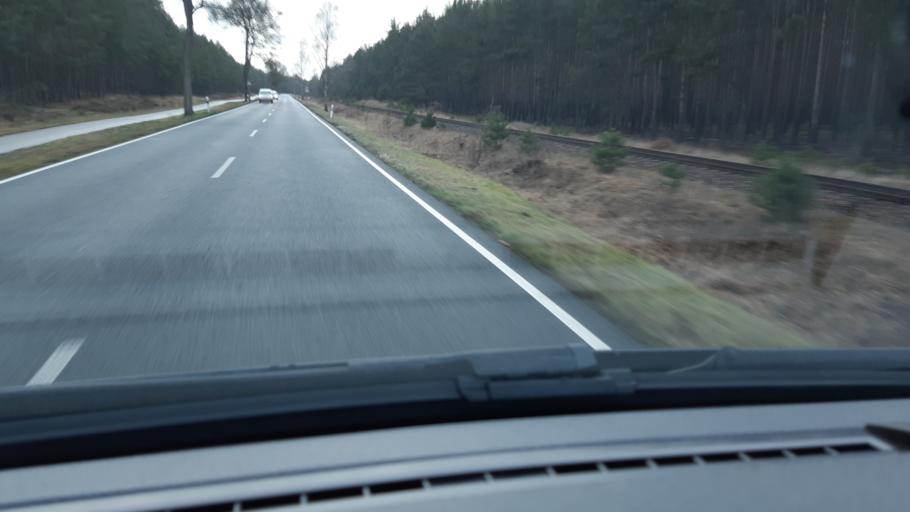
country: DE
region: Brandenburg
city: Zehdenick
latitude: 53.0164
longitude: 13.3698
